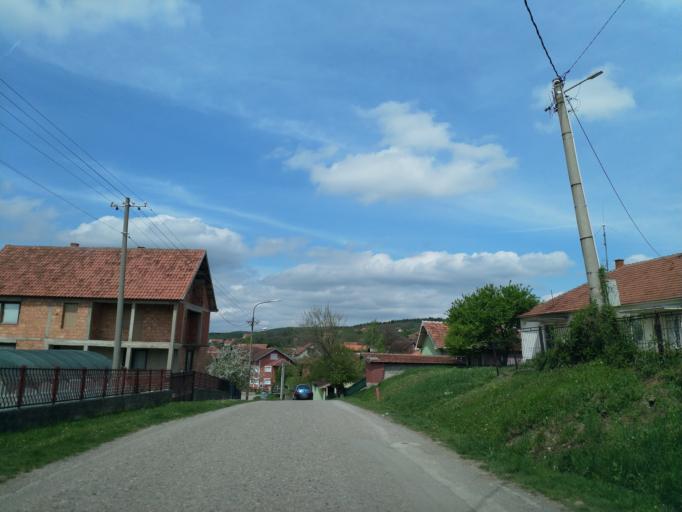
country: RS
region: Central Serbia
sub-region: Pomoravski Okrug
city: Paracin
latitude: 43.9412
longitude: 21.4945
